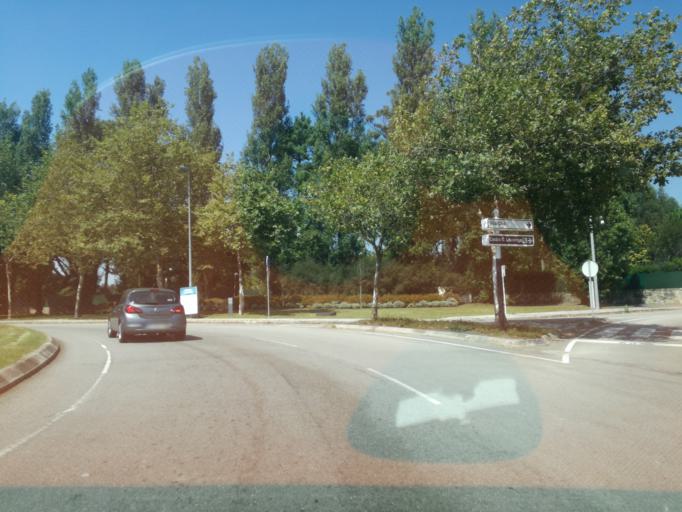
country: PT
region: Braga
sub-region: Esposende
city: Esposende
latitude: 41.5396
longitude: -8.7814
